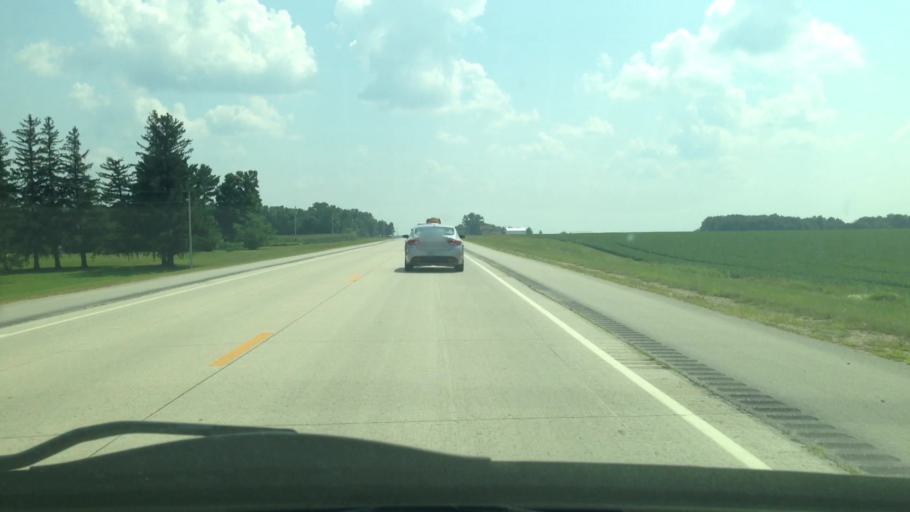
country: US
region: Minnesota
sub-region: Fillmore County
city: Spring Valley
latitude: 43.5220
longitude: -92.3694
